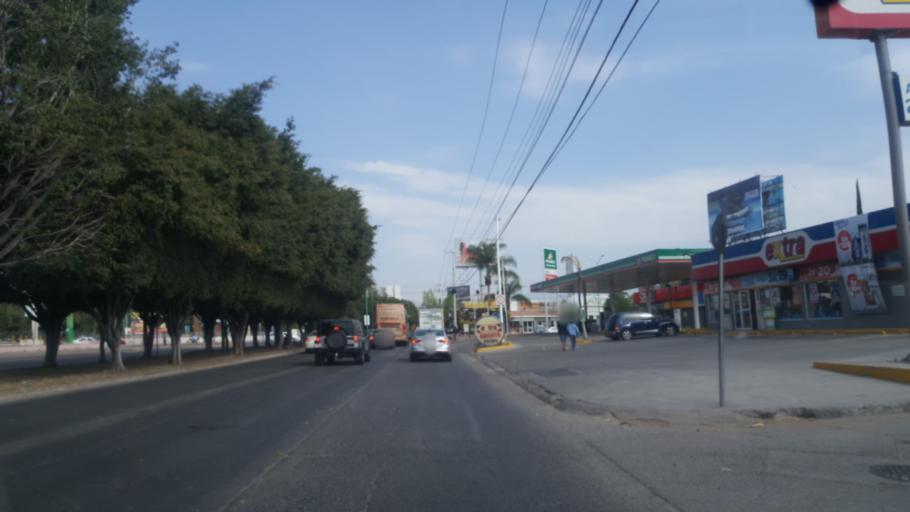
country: MX
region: Guanajuato
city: Leon
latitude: 21.1058
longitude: -101.6582
